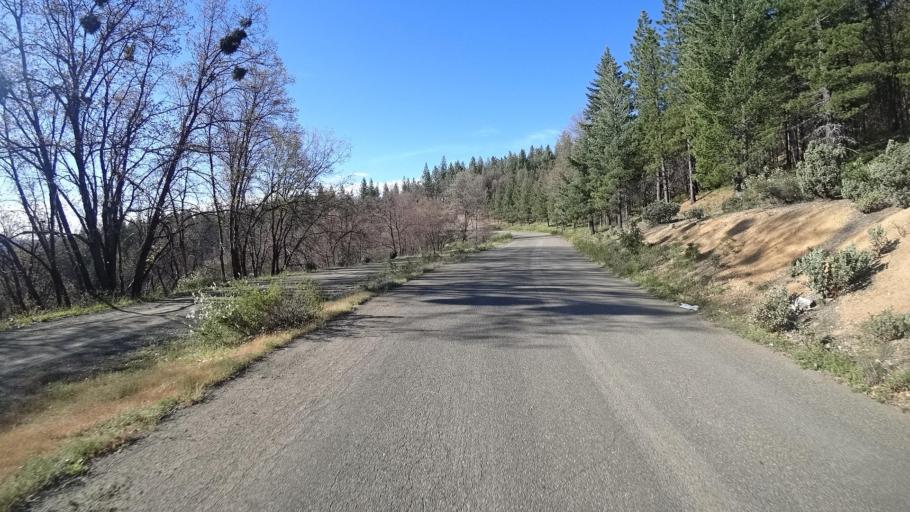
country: US
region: California
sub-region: Lake County
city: Upper Lake
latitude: 39.3149
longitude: -122.9468
